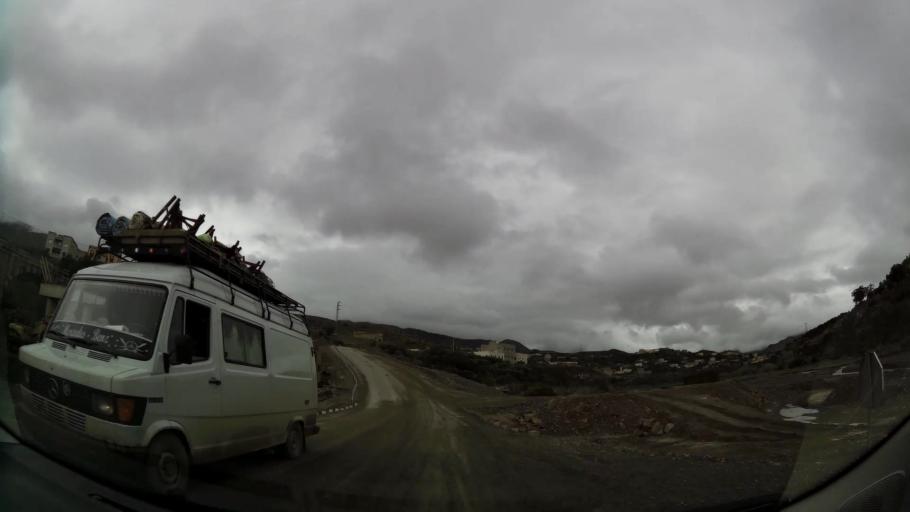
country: MA
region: Taza-Al Hoceima-Taounate
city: Imzourene
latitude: 34.9614
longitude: -3.8121
